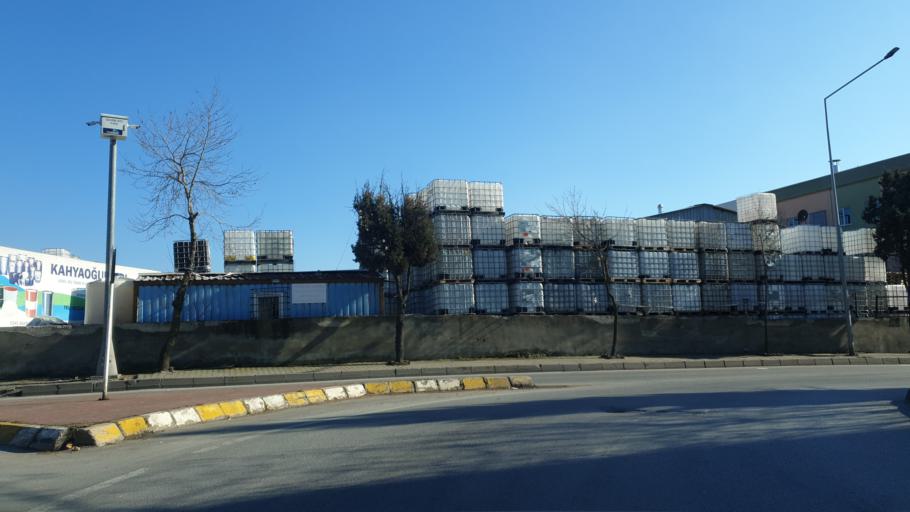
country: TR
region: Kocaeli
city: Balcik
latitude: 40.8806
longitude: 29.3709
